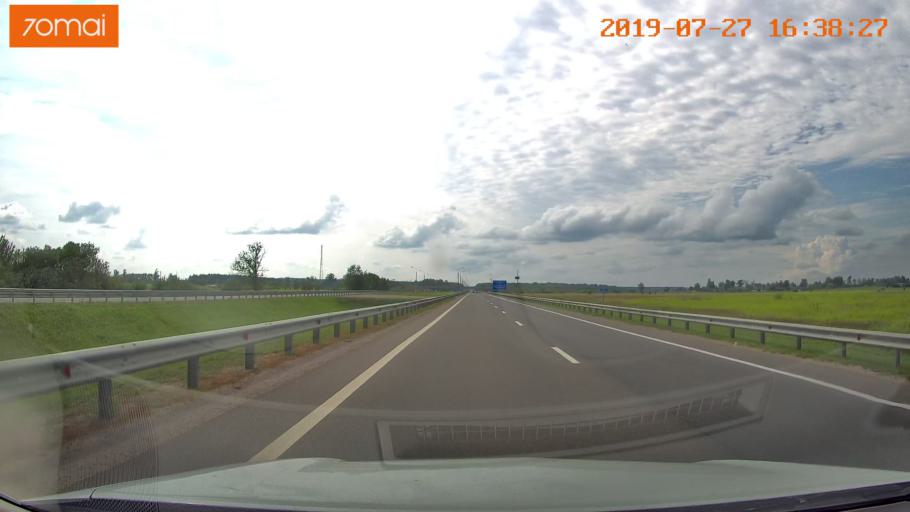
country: RU
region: Kaliningrad
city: Gvardeysk
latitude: 54.6489
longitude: 21.2276
